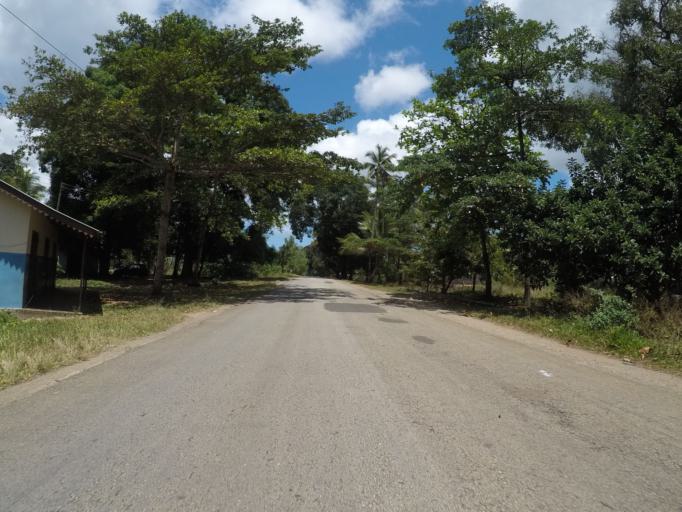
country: TZ
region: Zanzibar Central/South
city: Nganane
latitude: -6.2947
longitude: 39.4372
